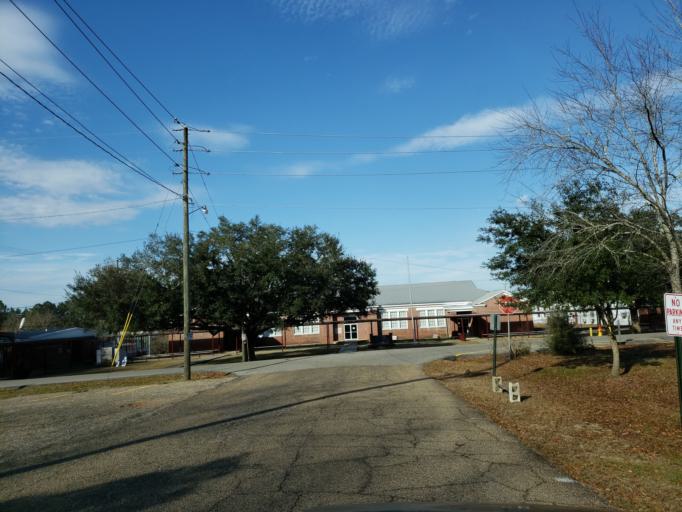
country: US
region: Mississippi
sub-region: Perry County
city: Richton
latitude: 31.3500
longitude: -88.9424
